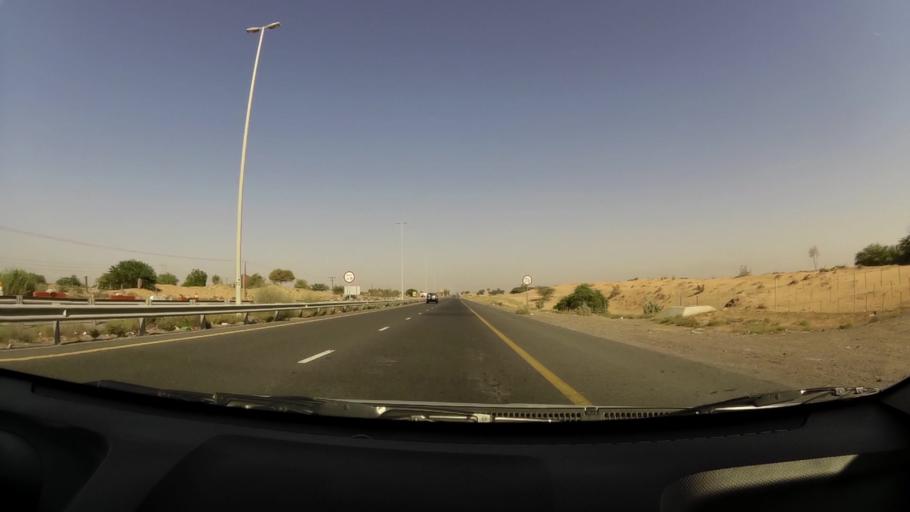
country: AE
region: Umm al Qaywayn
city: Umm al Qaywayn
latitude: 25.4676
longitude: 55.5909
